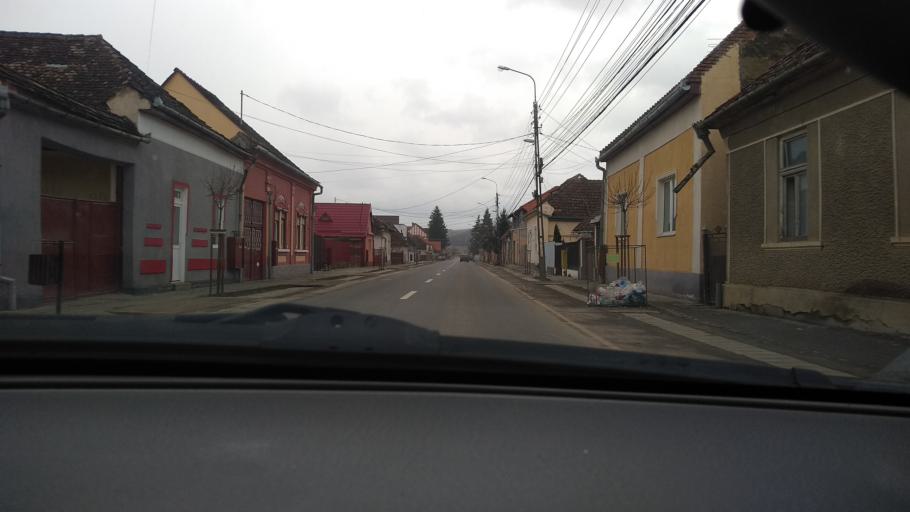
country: RO
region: Mures
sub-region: Comuna Miercurea Nirajului
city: Miercurea Nirajului
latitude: 46.5330
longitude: 24.7939
